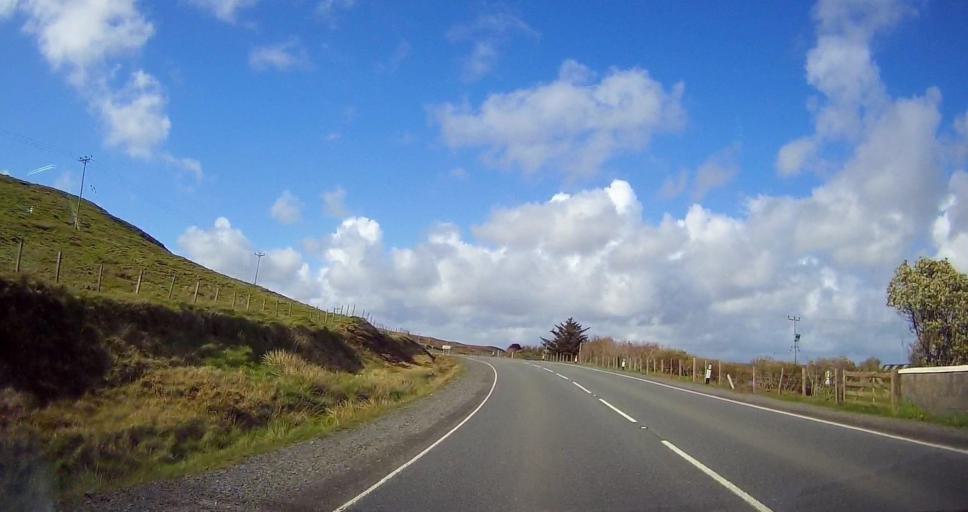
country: GB
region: Scotland
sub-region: Shetland Islands
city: Lerwick
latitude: 60.2398
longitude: -1.2290
